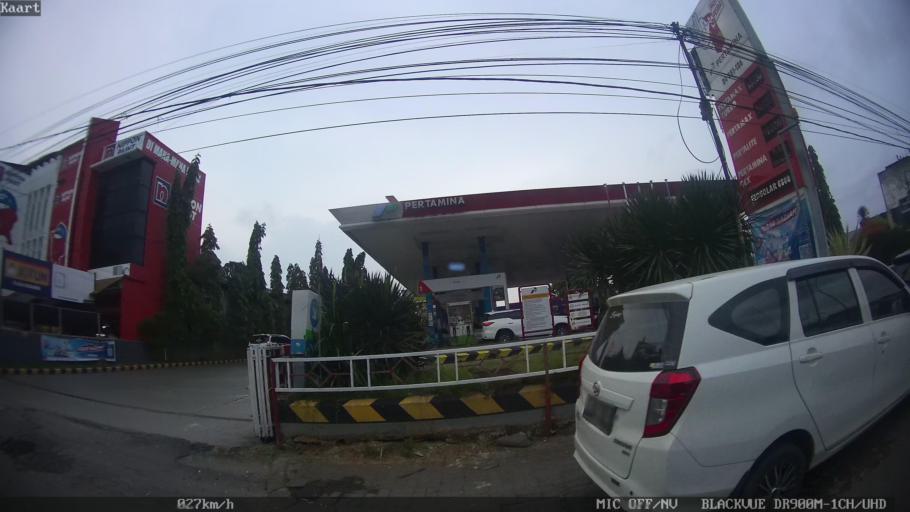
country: ID
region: Lampung
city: Bandarlampung
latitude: -5.4062
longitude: 105.2733
